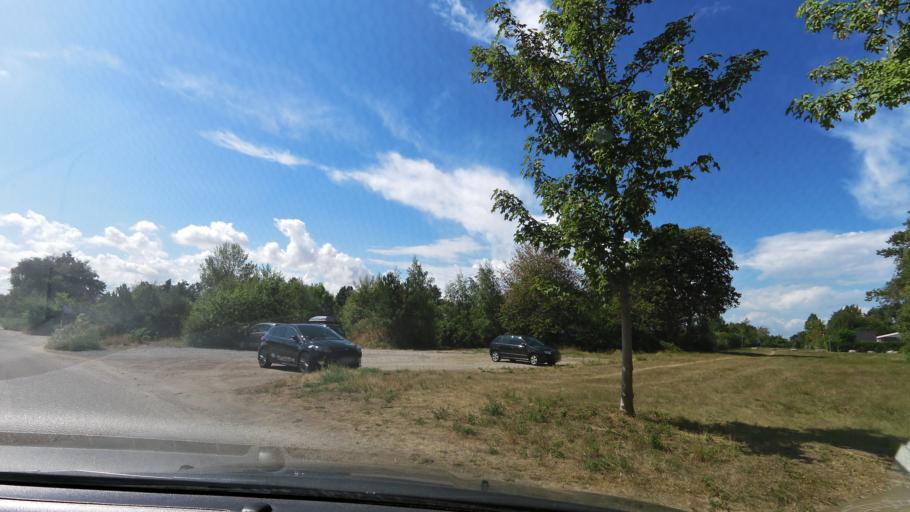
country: DK
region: South Denmark
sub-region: Nordfyns Kommune
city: Otterup
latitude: 55.5490
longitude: 10.4918
